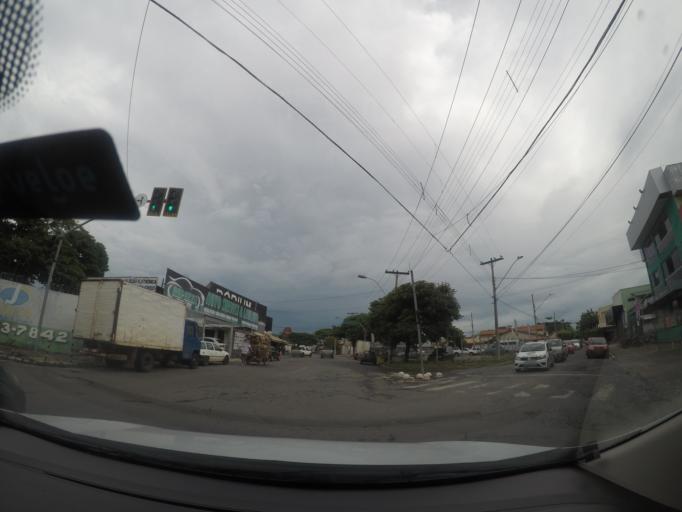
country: BR
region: Goias
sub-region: Goiania
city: Goiania
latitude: -16.6666
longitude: -49.2879
